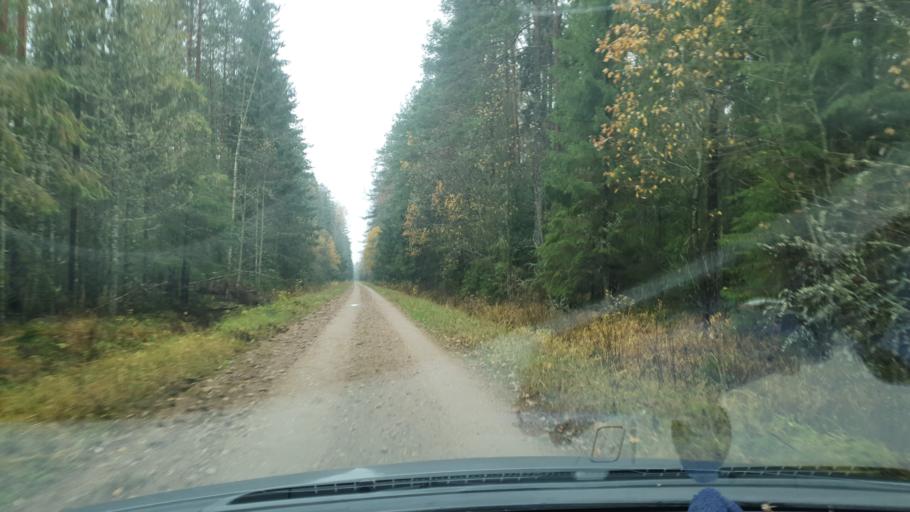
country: EE
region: Viljandimaa
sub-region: Karksi vald
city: Karksi-Nuia
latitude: 57.9788
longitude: 25.6259
